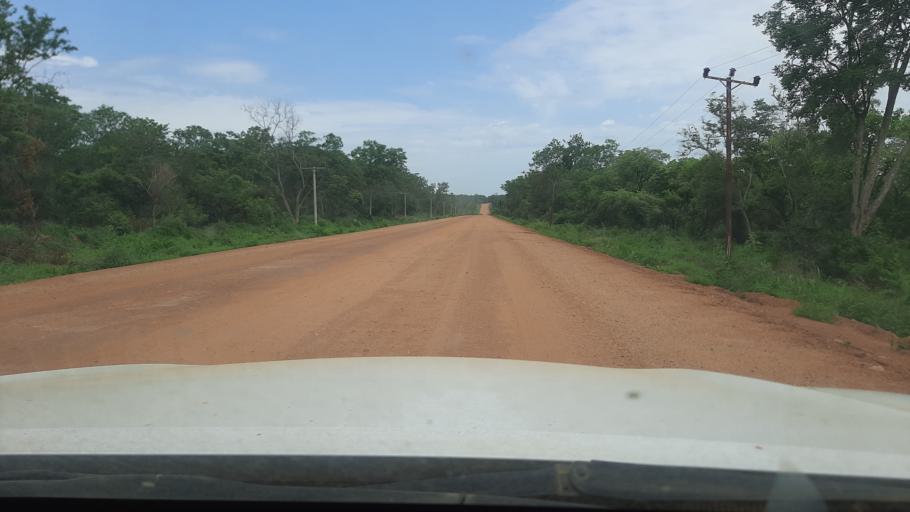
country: ET
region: Gambela
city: Gambela
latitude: 8.0966
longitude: 34.5879
